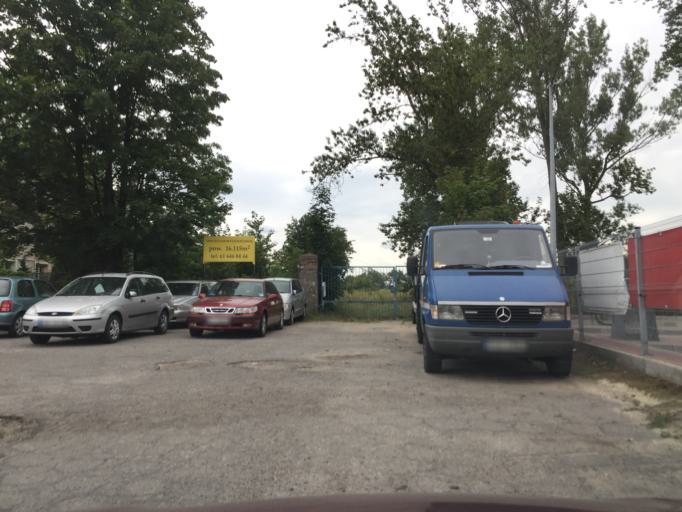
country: PL
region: Greater Poland Voivodeship
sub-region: Kalisz
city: Kalisz
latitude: 51.7414
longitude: 18.0608
